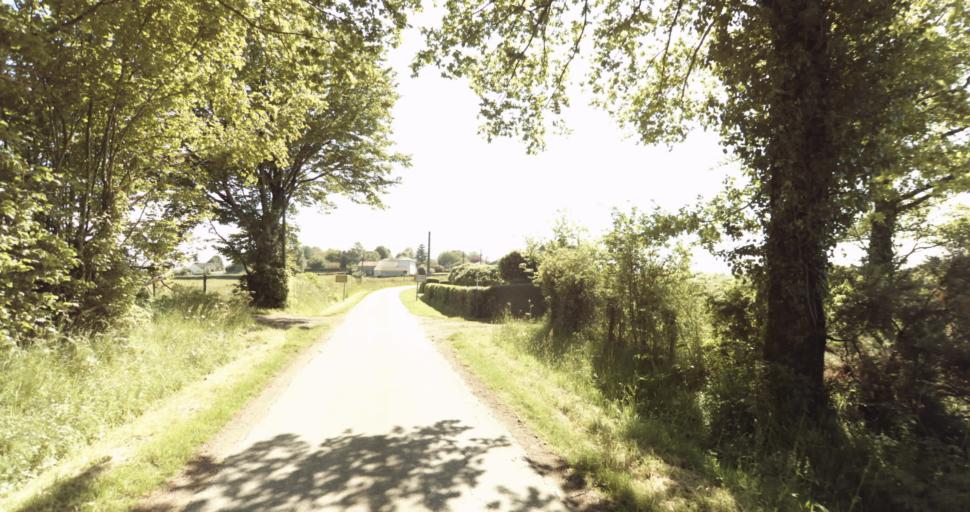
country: FR
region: Limousin
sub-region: Departement de la Haute-Vienne
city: Le Vigen
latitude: 45.7317
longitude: 1.2793
